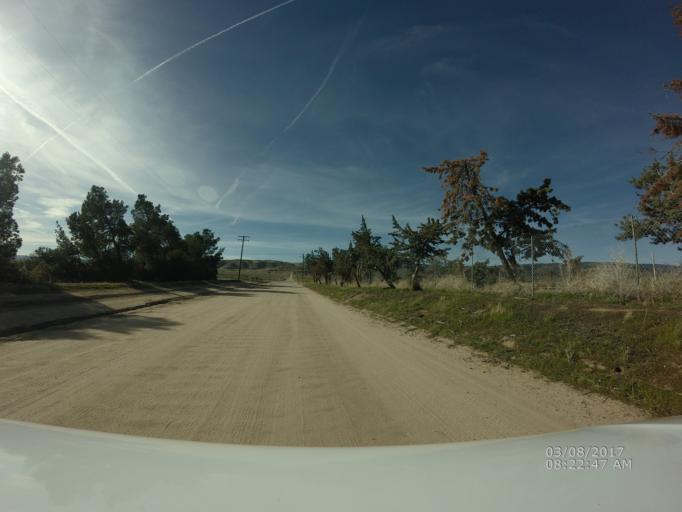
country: US
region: California
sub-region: Los Angeles County
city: Green Valley
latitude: 34.7398
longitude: -118.4487
